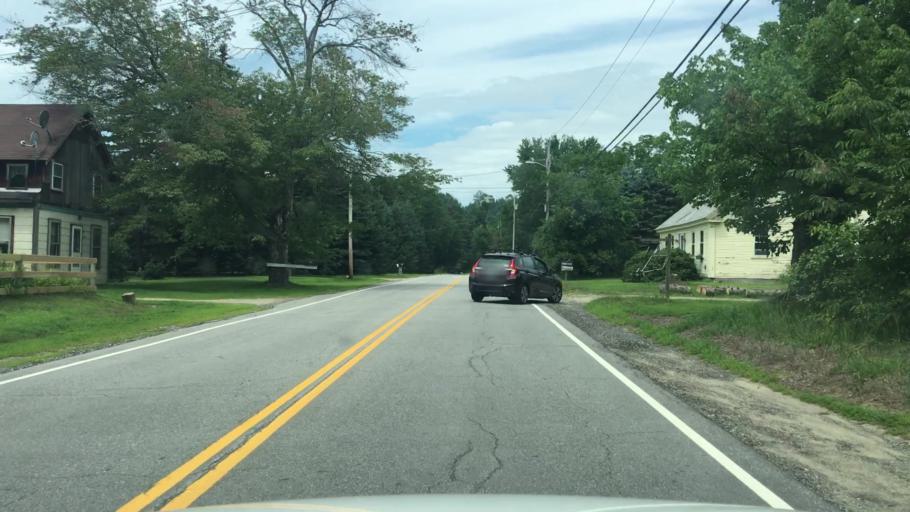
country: US
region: New Hampshire
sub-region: Grafton County
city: Rumney
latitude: 43.7919
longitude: -71.7821
